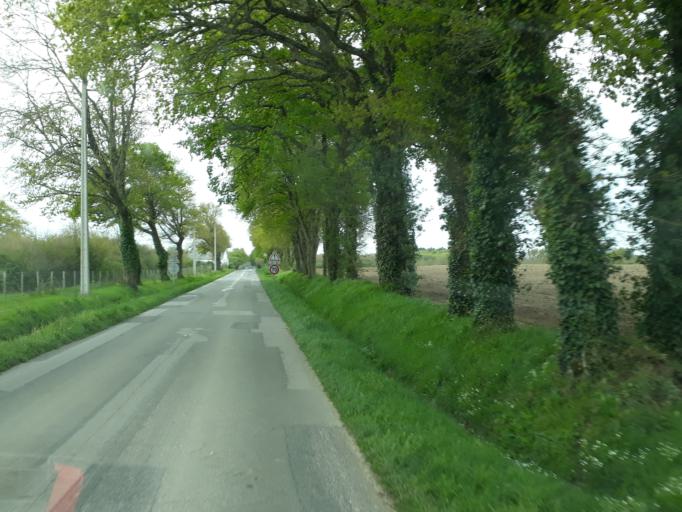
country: FR
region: Brittany
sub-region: Departement du Morbihan
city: Theix
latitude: 47.6224
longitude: -2.6774
